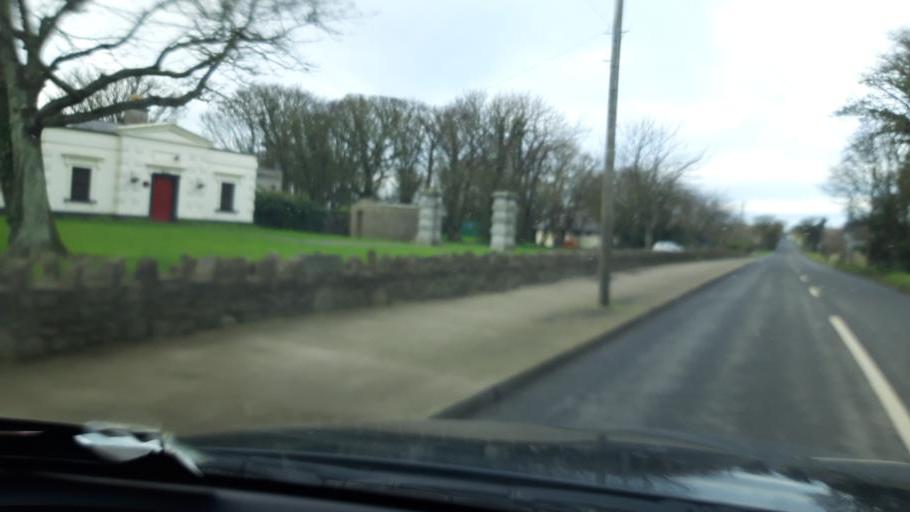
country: IE
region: Leinster
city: An Ros
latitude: 53.5395
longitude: -6.0931
